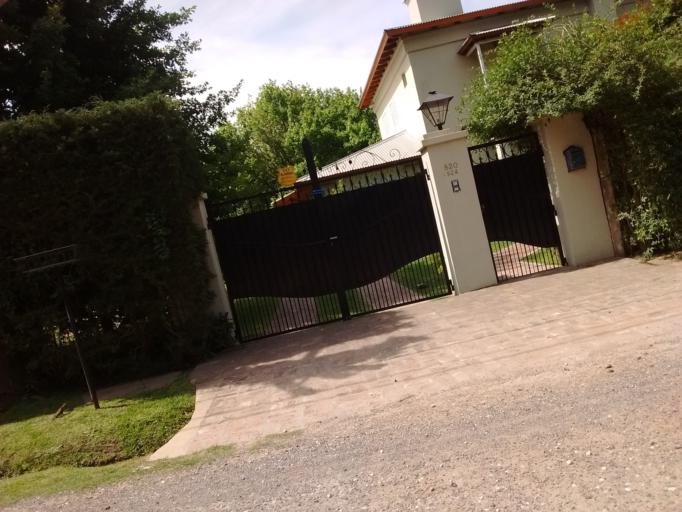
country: AR
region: Santa Fe
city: Funes
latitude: -32.9166
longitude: -60.7996
